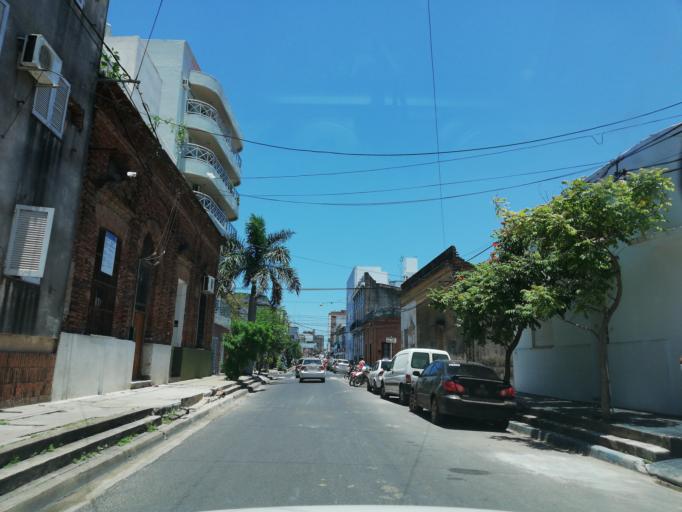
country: AR
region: Corrientes
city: Corrientes
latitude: -27.4618
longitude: -58.8337
